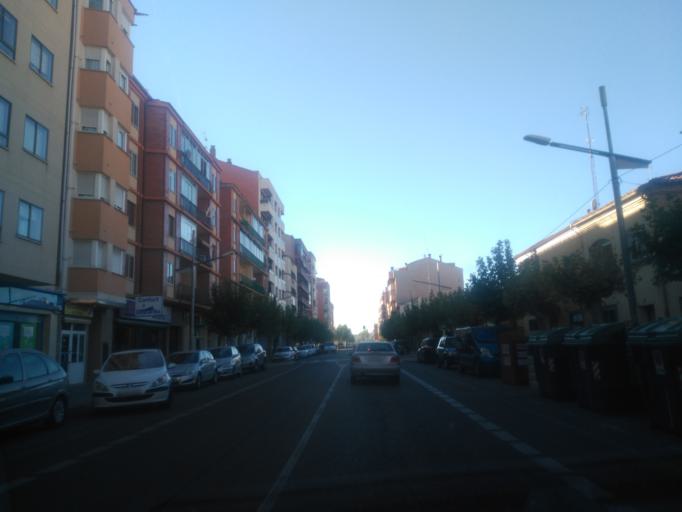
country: ES
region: Castille and Leon
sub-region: Provincia de Burgos
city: Aranda de Duero
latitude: 41.6674
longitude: -3.6910
